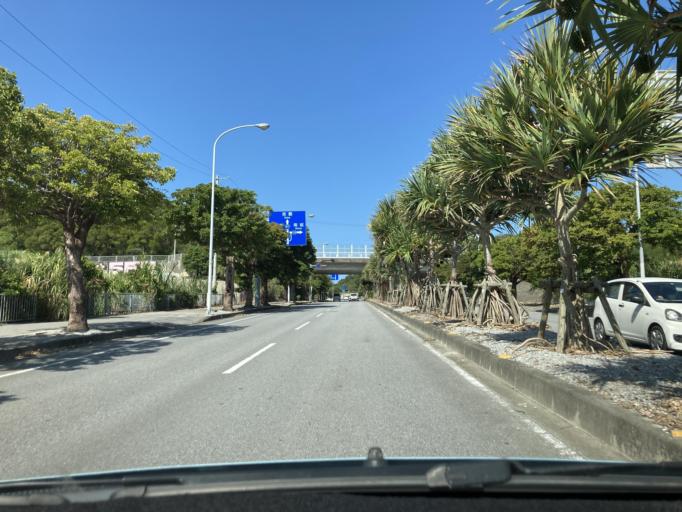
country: JP
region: Okinawa
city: Tomigusuku
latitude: 26.1829
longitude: 127.7230
